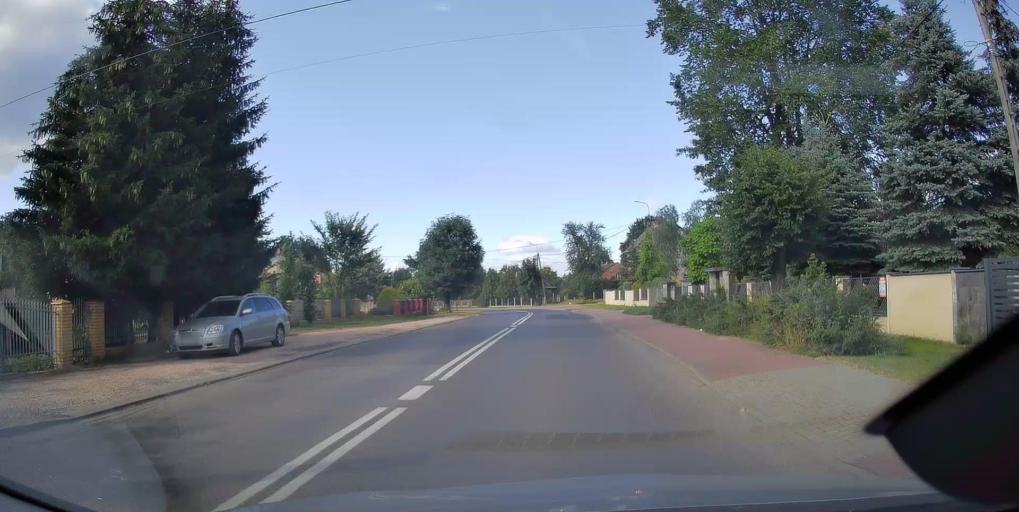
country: PL
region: Swietokrzyskie
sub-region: Powiat skarzyski
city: Suchedniow
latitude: 51.0310
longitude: 20.8394
